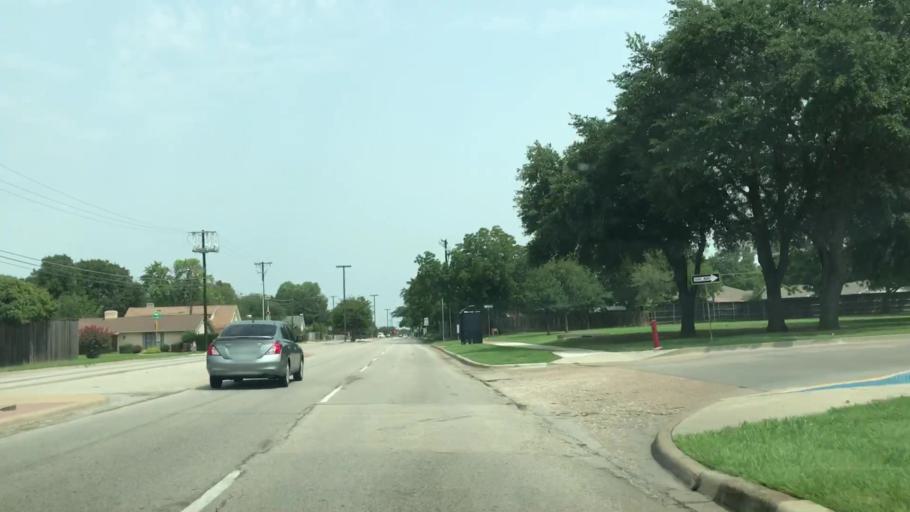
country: US
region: Texas
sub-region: Dallas County
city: Irving
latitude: 32.8544
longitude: -96.9590
